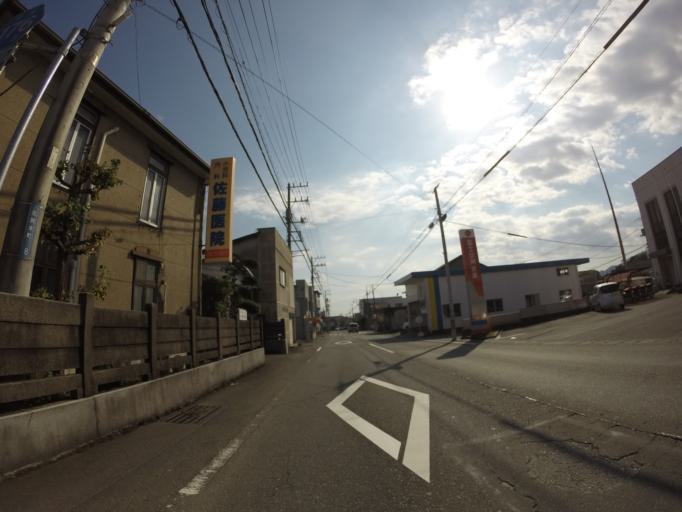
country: JP
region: Shizuoka
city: Fujinomiya
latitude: 35.1872
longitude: 138.6463
